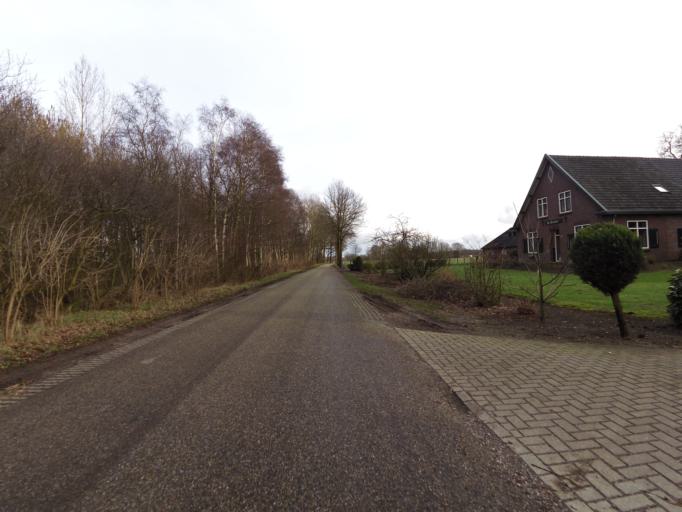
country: NL
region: Gelderland
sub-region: Oude IJsselstreek
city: Wisch
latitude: 51.9737
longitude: 6.4126
